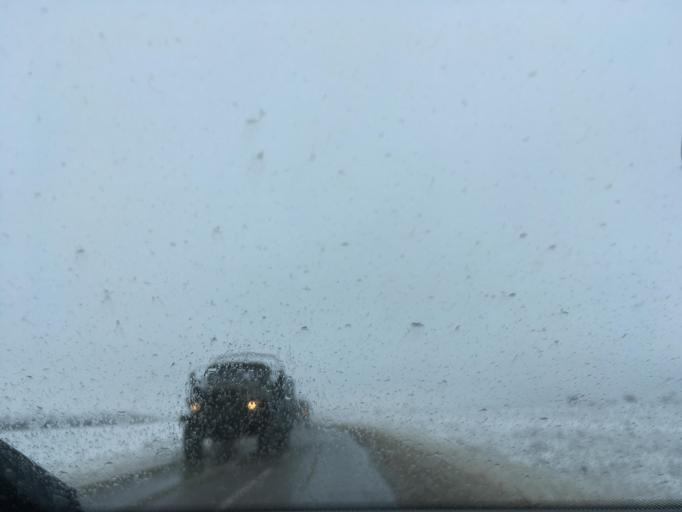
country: RU
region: Voronezj
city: Ol'khovatka
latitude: 50.1280
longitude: 39.1899
